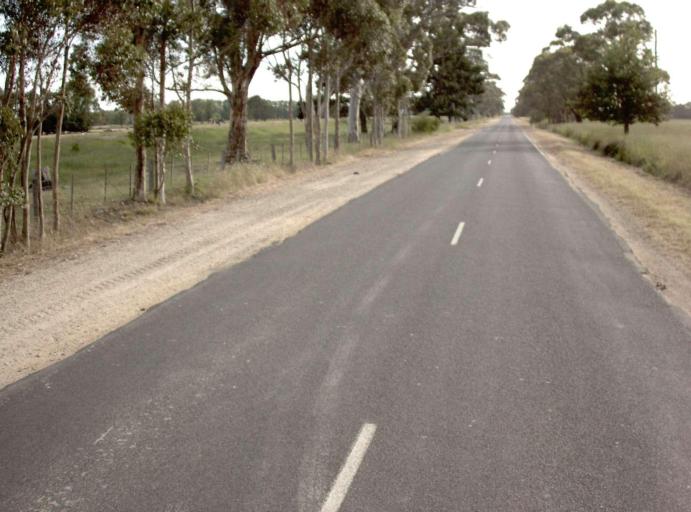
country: AU
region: Victoria
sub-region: Wellington
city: Heyfield
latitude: -38.0109
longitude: 146.7773
